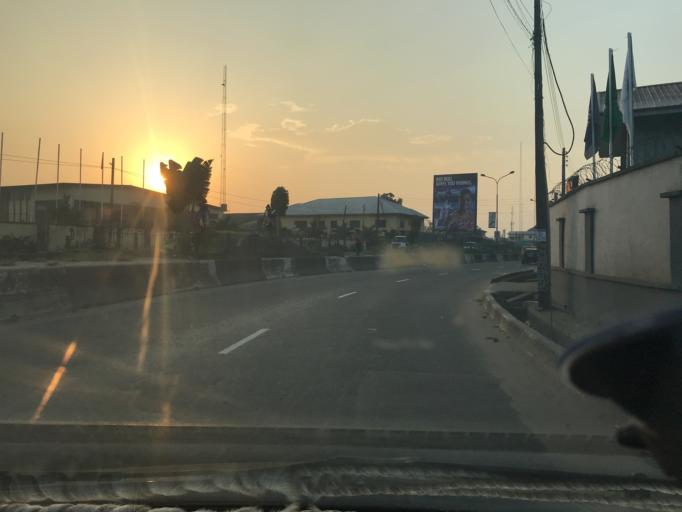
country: NG
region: Lagos
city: Makoko
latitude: 6.4971
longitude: 3.3799
